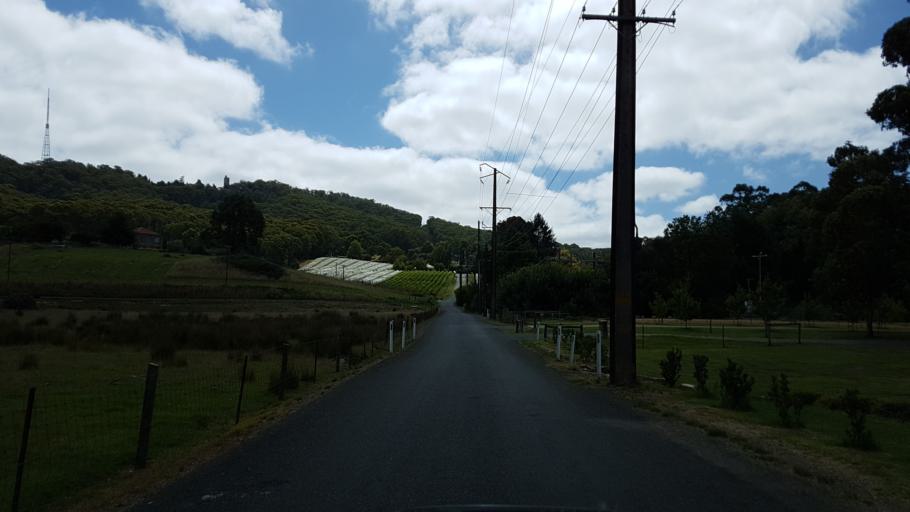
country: AU
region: South Australia
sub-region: Adelaide Hills
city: Crafers
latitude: -34.9827
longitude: 138.7219
